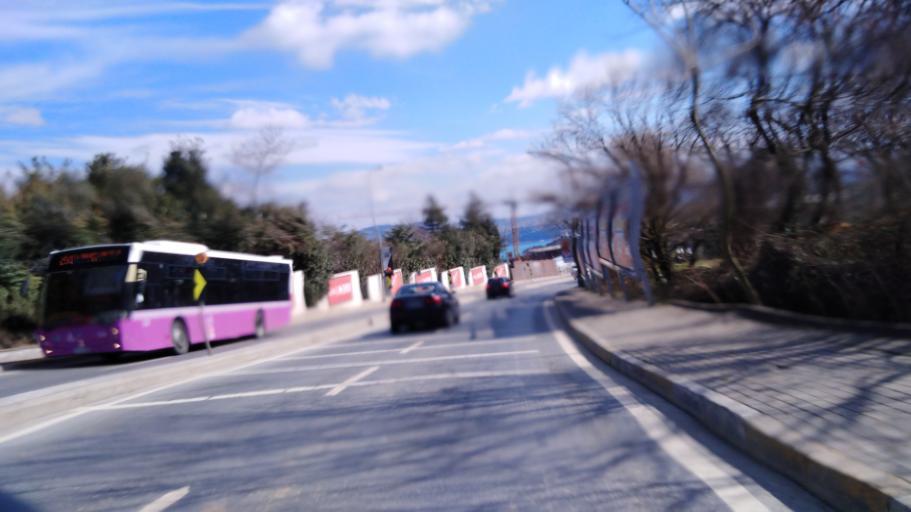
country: TR
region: Istanbul
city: Sisli
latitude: 41.1124
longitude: 29.0431
